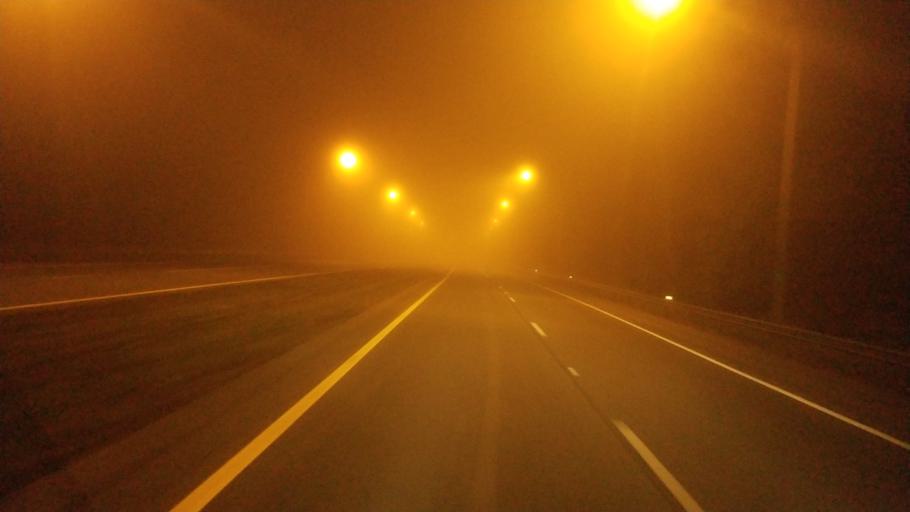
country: US
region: Ohio
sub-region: Scioto County
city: West Portsmouth
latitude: 38.7437
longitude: -83.0255
